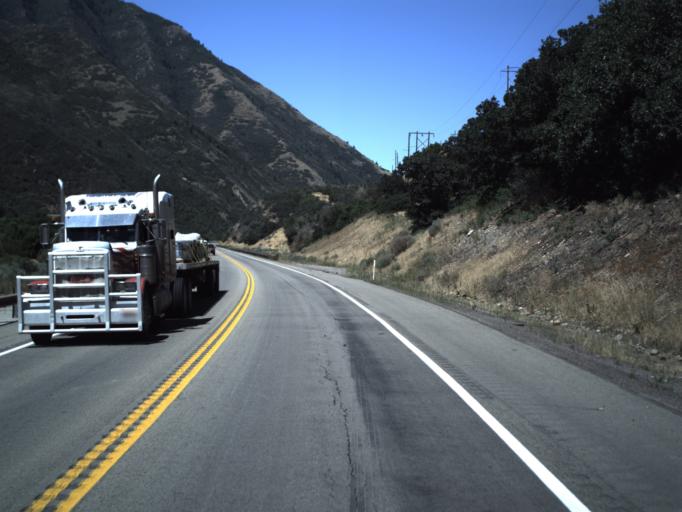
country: US
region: Utah
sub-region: Utah County
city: Mapleton
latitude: 40.0545
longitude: -111.5509
